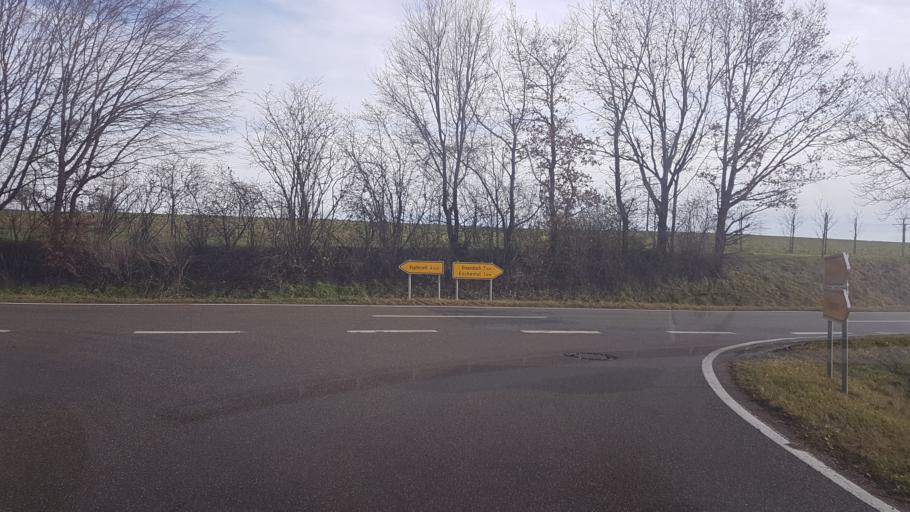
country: DE
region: Baden-Wuerttemberg
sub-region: Regierungsbezirk Stuttgart
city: Kupferzell
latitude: 49.2108
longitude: 9.7332
